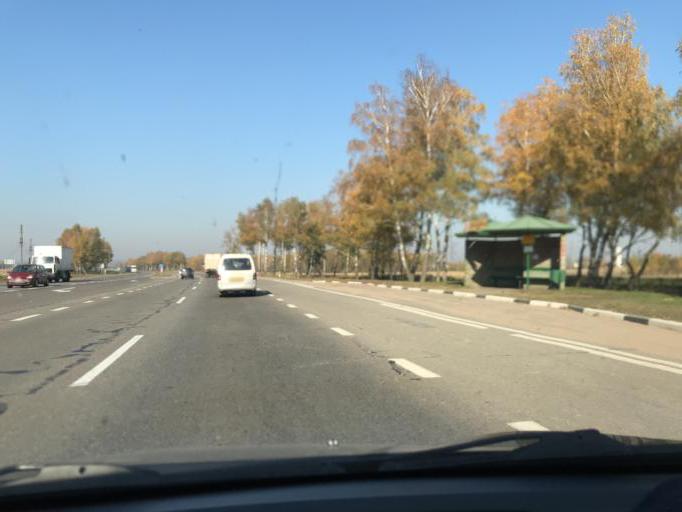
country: BY
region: Minsk
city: Luhavaya Slabada
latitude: 53.7742
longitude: 27.8272
